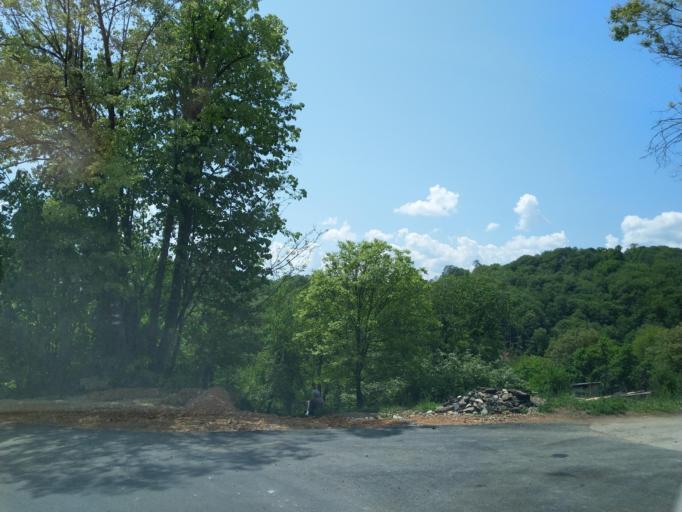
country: RS
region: Central Serbia
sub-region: Zlatiborski Okrug
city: Uzice
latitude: 43.8580
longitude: 19.9240
